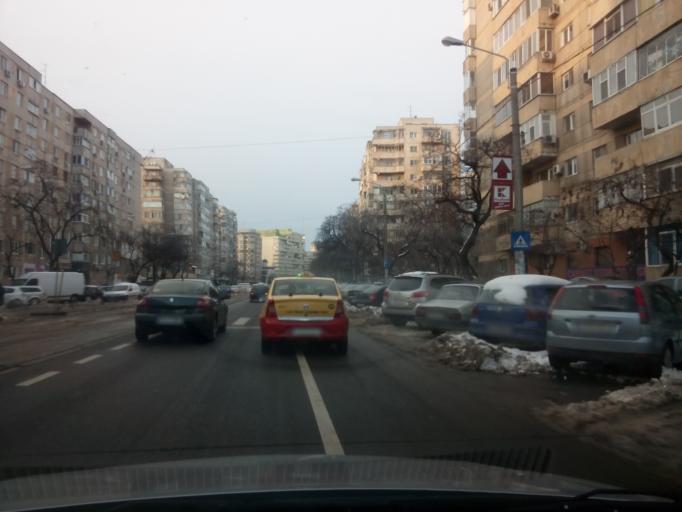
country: RO
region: Ilfov
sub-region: Comuna Fundeni-Dobroesti
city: Fundeni
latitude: 44.4384
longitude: 26.1587
